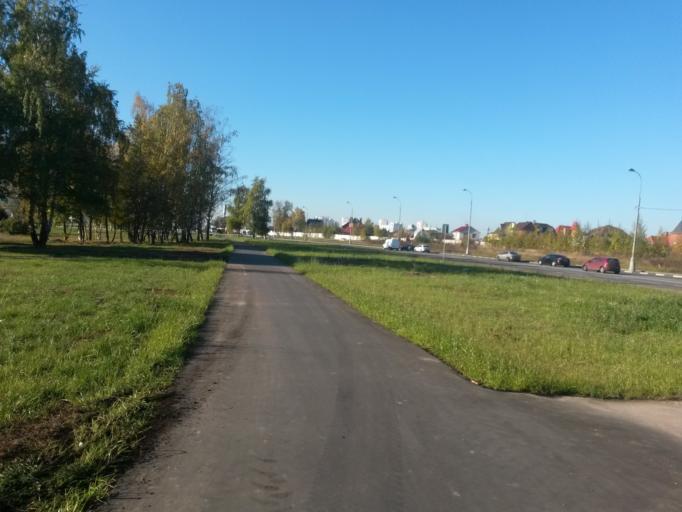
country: RU
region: Moskovskaya
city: Kommunarka
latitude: 55.5463
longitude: 37.5150
